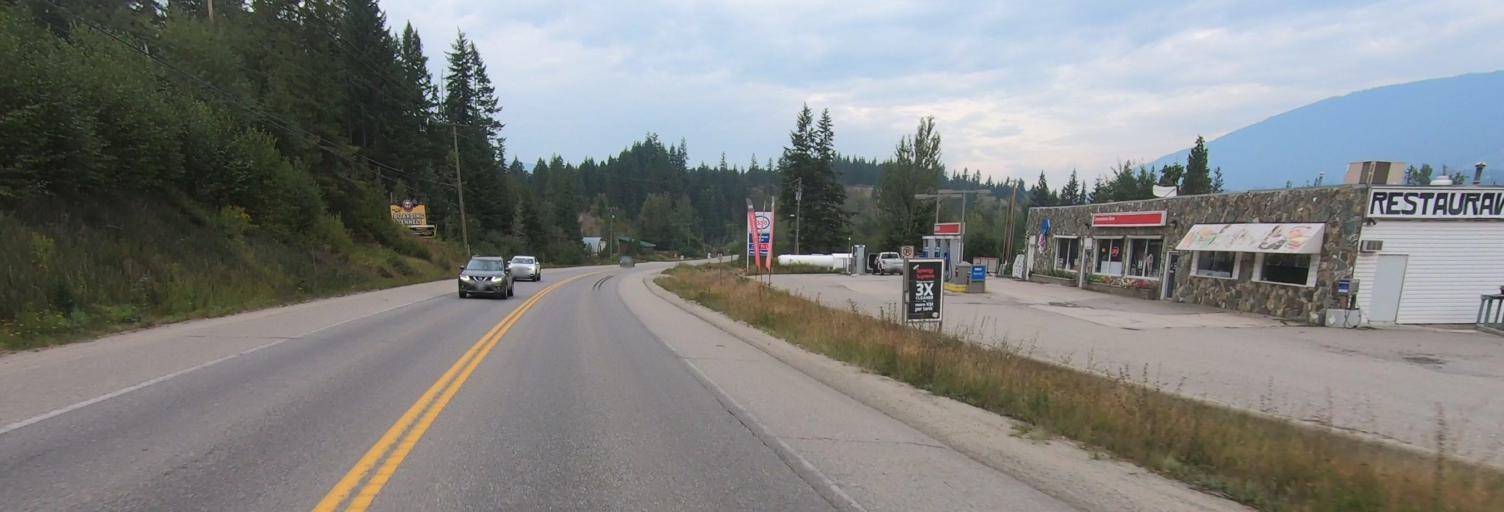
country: CA
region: British Columbia
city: Salmon Arm
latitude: 50.7725
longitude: -119.3398
